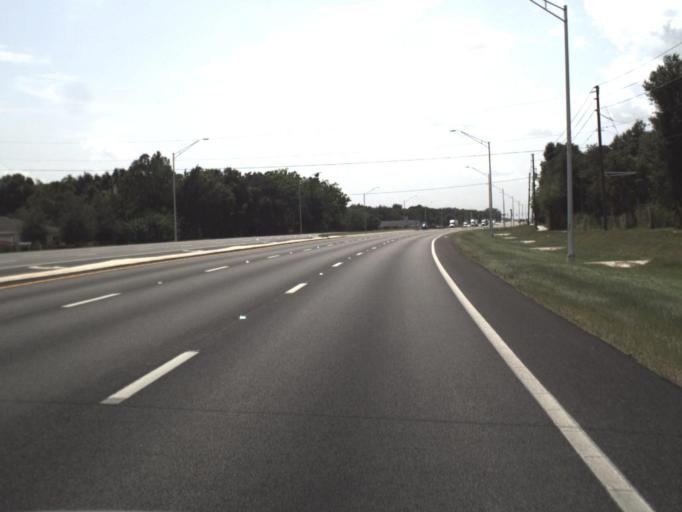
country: US
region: Florida
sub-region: Highlands County
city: Avon Park
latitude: 27.6246
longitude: -81.5149
